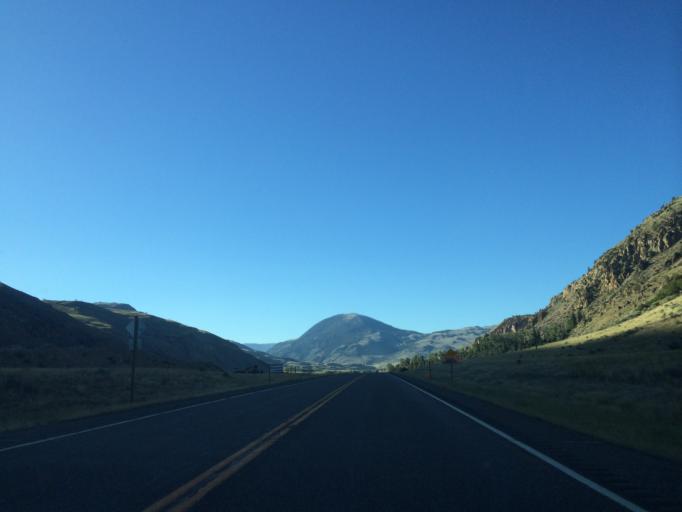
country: US
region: Montana
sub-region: Gallatin County
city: West Yellowstone
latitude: 45.1034
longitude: -110.7826
